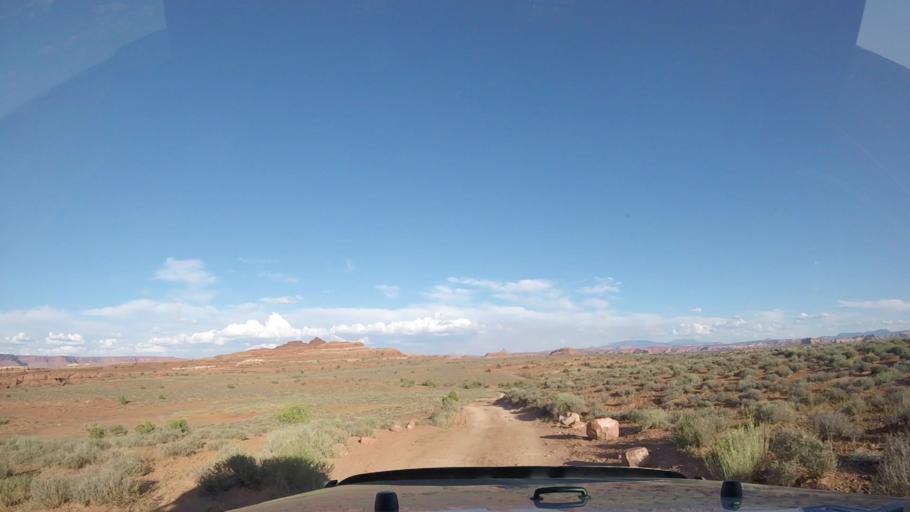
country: US
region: Utah
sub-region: Grand County
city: Moab
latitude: 38.2131
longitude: -109.7903
